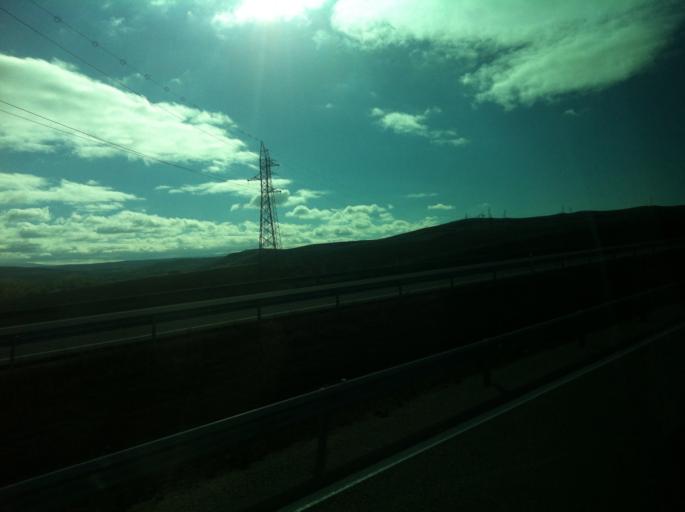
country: ES
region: Castille and Leon
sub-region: Provincia de Burgos
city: Monasterio de Rodilla
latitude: 42.4587
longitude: -3.4527
